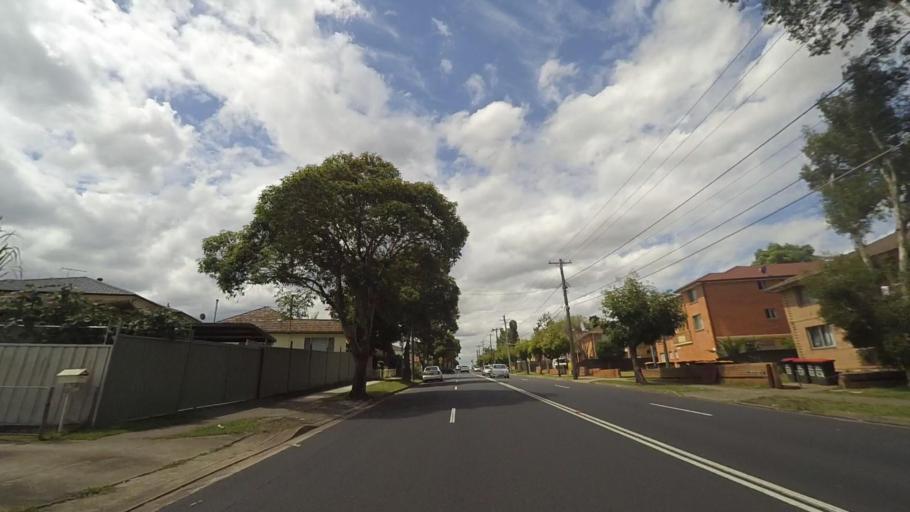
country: AU
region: New South Wales
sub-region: Fairfield
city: Fairfield Heights
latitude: -33.8686
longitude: 150.9481
